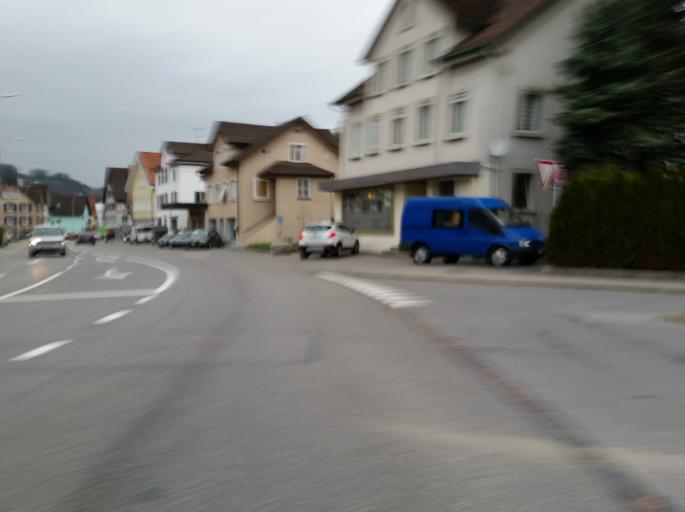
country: CH
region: Saint Gallen
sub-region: Wahlkreis Rheintal
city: Sankt Margrethen
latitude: 47.4534
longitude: 9.6313
